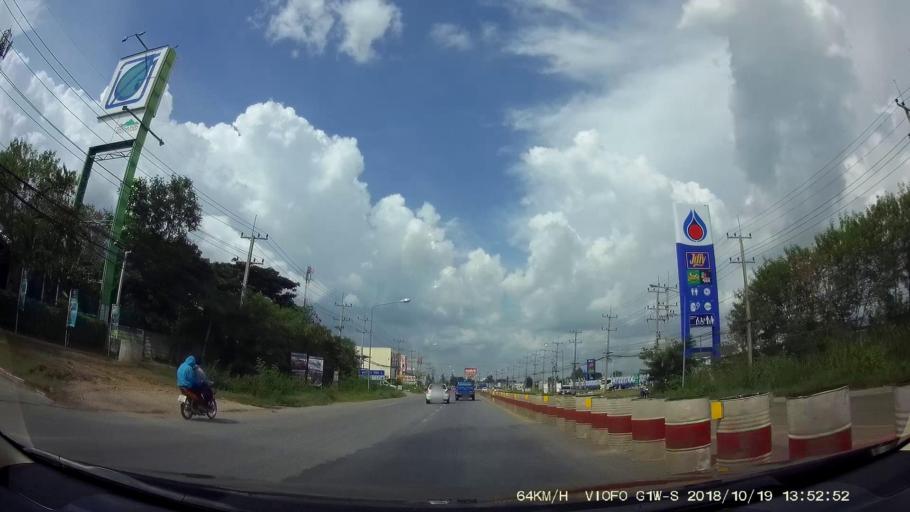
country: TH
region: Chaiyaphum
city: Chaiyaphum
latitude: 15.7716
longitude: 102.0257
